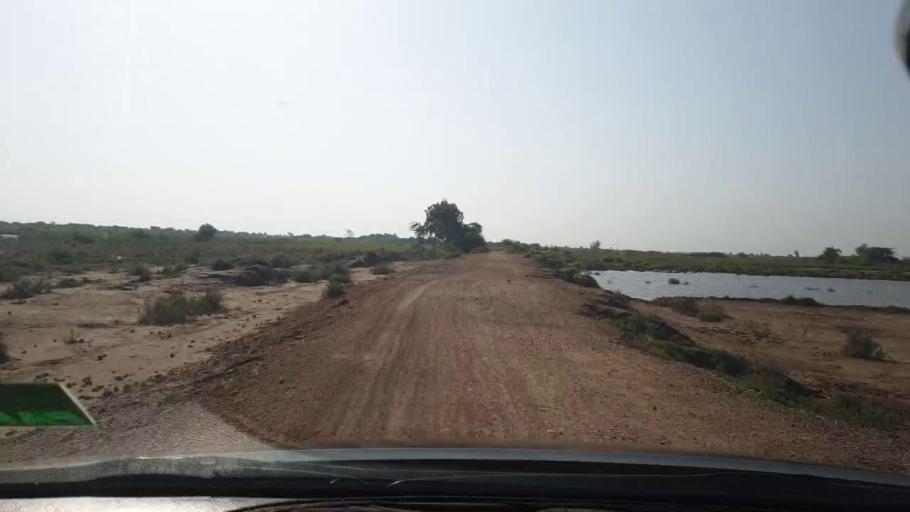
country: PK
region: Sindh
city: Tando Bago
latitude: 24.7172
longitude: 68.9688
